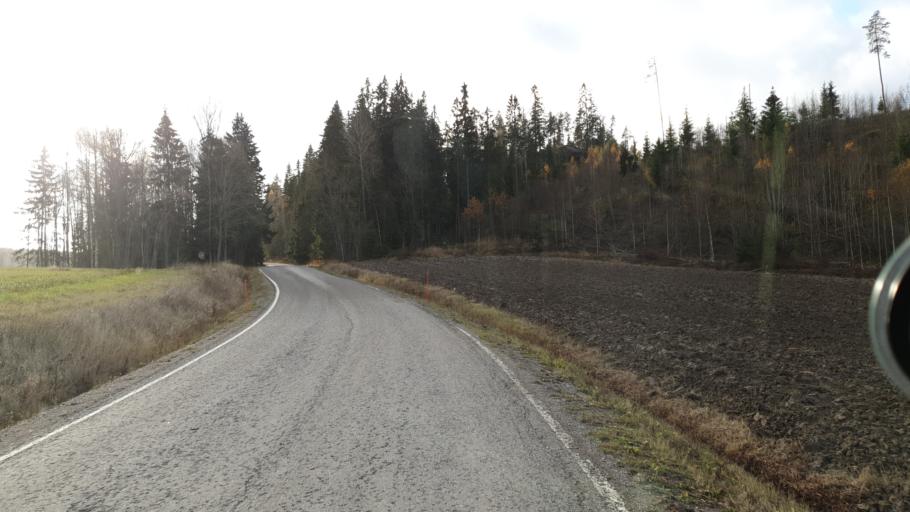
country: FI
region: Uusimaa
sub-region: Helsinki
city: Siuntio
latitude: 60.2523
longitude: 24.2986
